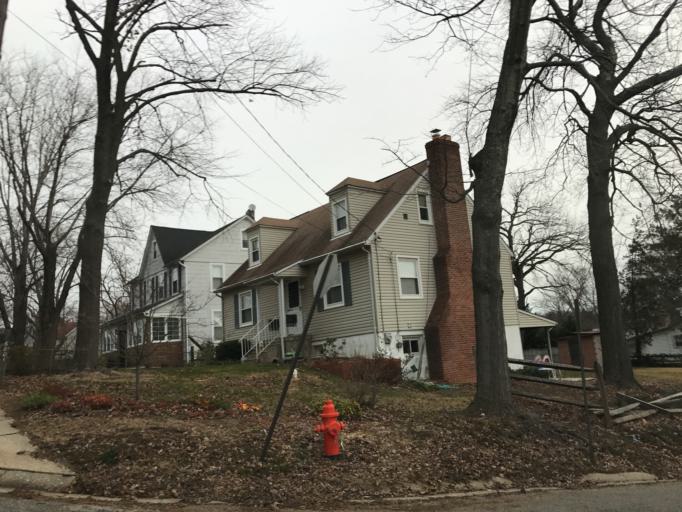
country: US
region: Maryland
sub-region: Baltimore County
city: Overlea
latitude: 39.3593
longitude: -76.5368
